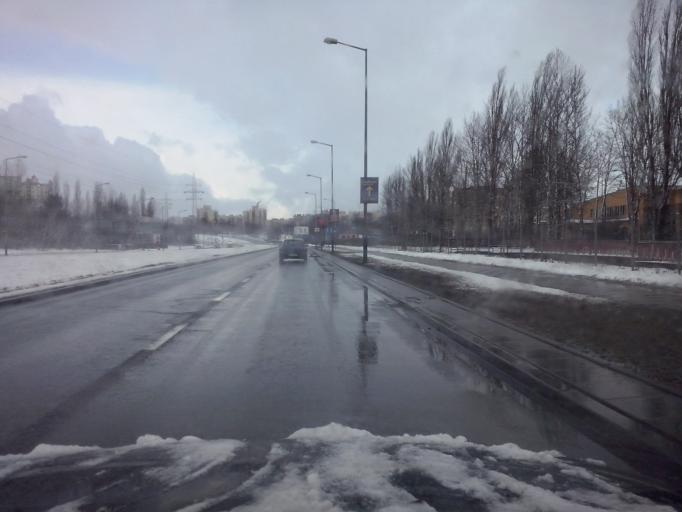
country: PL
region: Lesser Poland Voivodeship
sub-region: Krakow
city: Krakow
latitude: 50.0686
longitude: 20.0047
